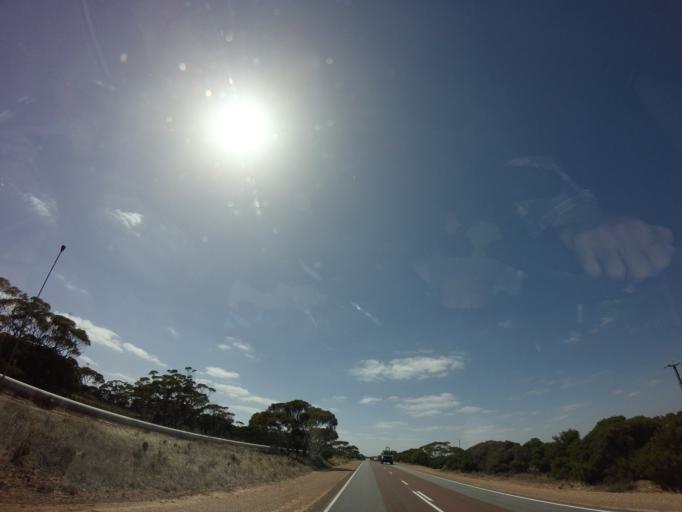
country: AU
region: South Australia
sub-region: Kimba
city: Caralue
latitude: -33.0829
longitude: 135.4988
